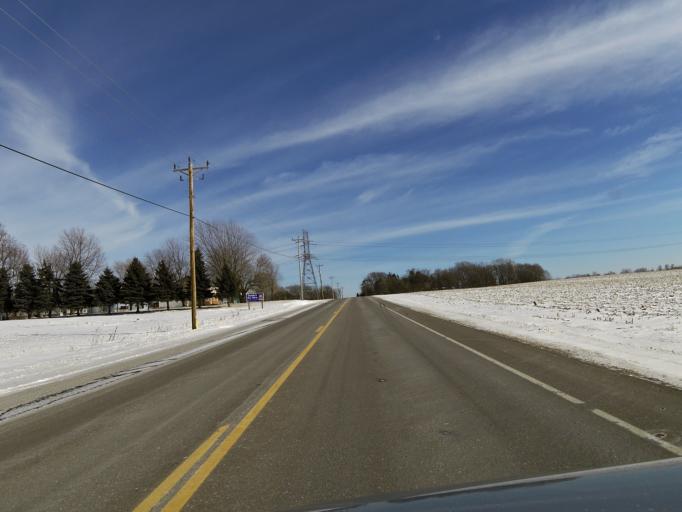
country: US
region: Minnesota
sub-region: Washington County
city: Afton
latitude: 44.8910
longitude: -92.8581
